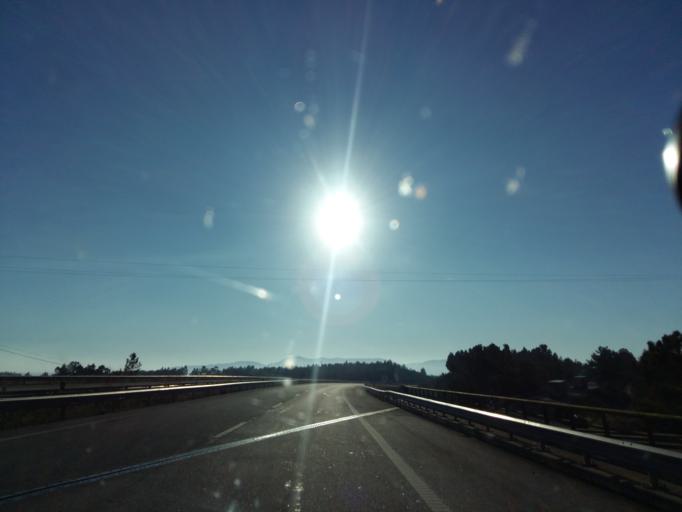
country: PT
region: Castelo Branco
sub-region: Castelo Branco
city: Castelo Branco
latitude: 39.7447
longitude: -7.6346
